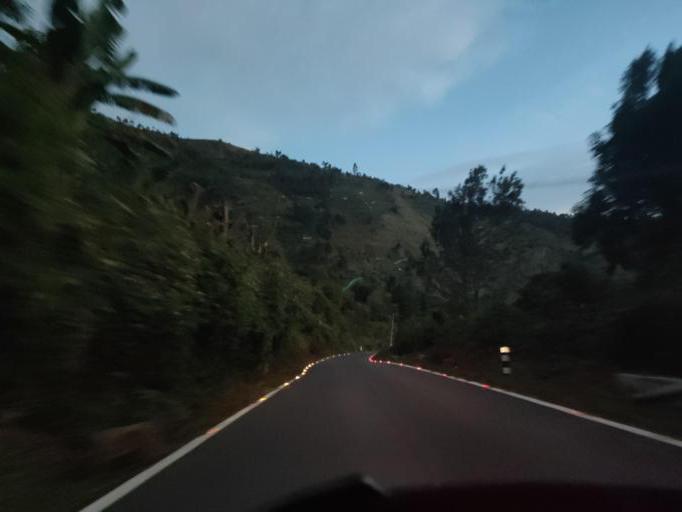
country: IN
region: Tamil Nadu
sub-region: Dindigul
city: Kodaikanal
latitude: 10.2880
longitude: 77.5387
